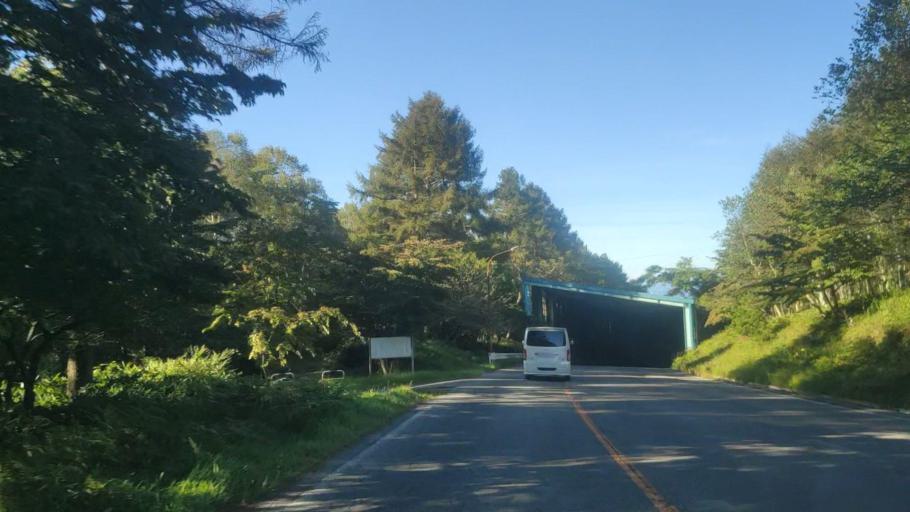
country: JP
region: Nagano
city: Kamimaruko
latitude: 36.1764
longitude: 138.2814
